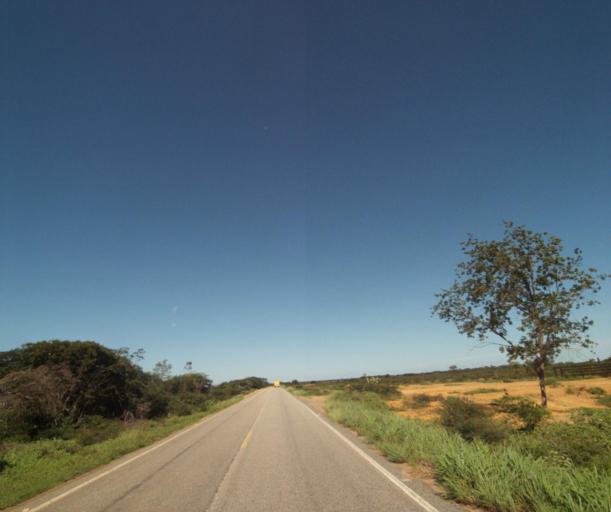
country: BR
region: Bahia
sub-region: Palmas De Monte Alto
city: Palmas de Monte Alto
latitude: -14.2569
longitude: -43.2540
